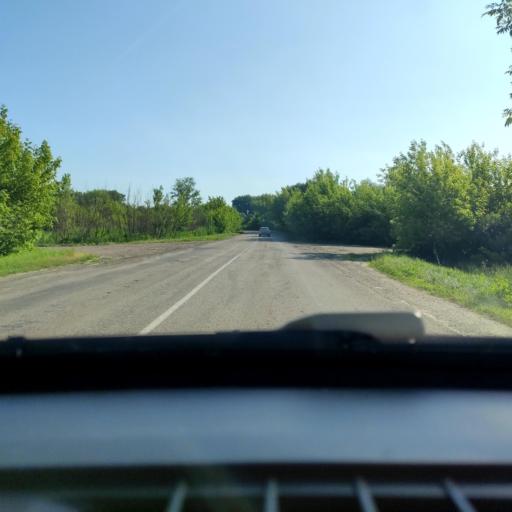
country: RU
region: Voronezj
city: Panino
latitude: 51.5992
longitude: 39.9788
